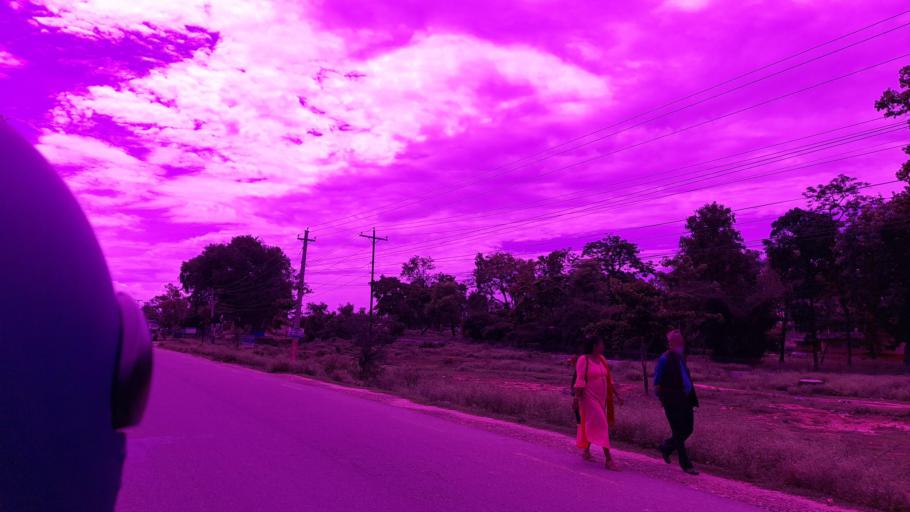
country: NP
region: Mid Western
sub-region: Bheri Zone
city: Nepalgunj
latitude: 28.1994
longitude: 81.6883
